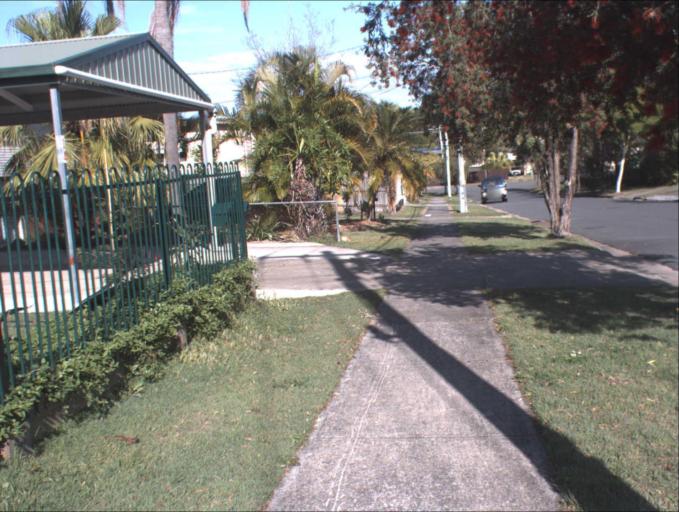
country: AU
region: Queensland
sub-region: Logan
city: Waterford West
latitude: -27.6833
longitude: 153.0957
